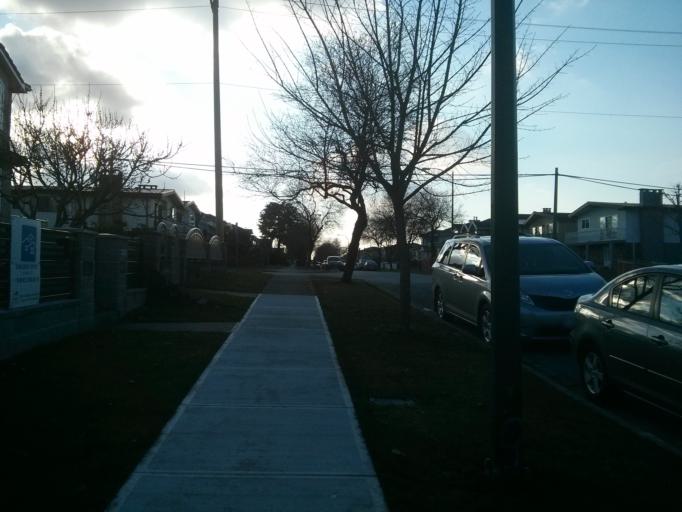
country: CA
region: British Columbia
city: Burnaby
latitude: 49.2479
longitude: -123.0279
